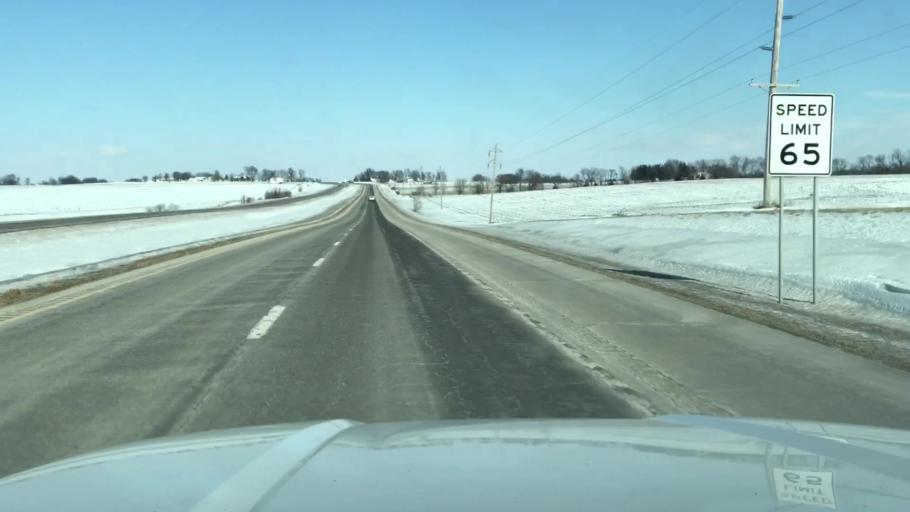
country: US
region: Missouri
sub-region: Nodaway County
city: Maryville
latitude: 40.2609
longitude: -94.8667
